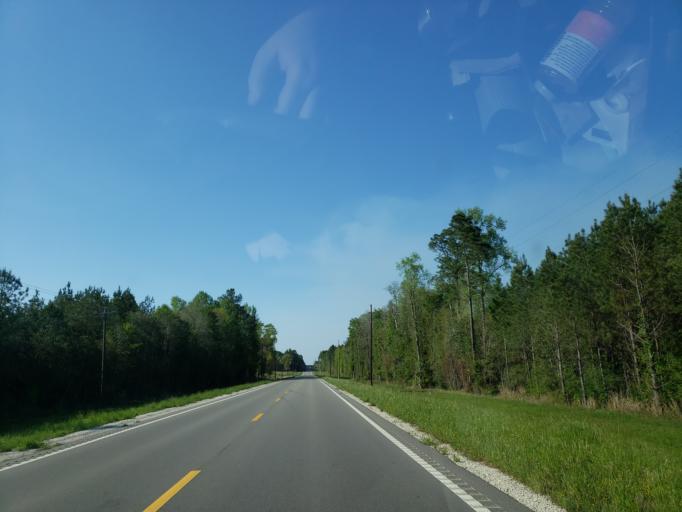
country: US
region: Mississippi
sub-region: Perry County
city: Richton
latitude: 31.2821
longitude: -88.9219
